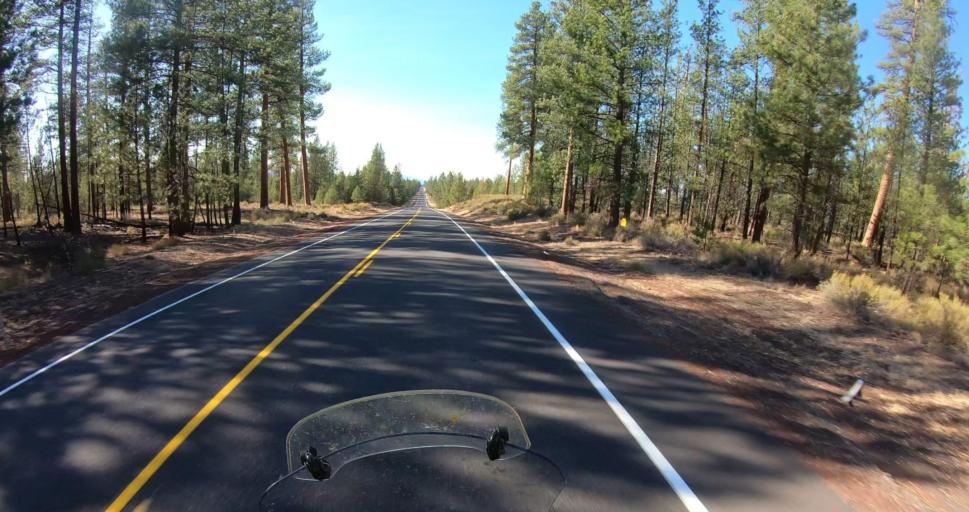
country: US
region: Oregon
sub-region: Deschutes County
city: La Pine
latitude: 43.4733
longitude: -121.4029
